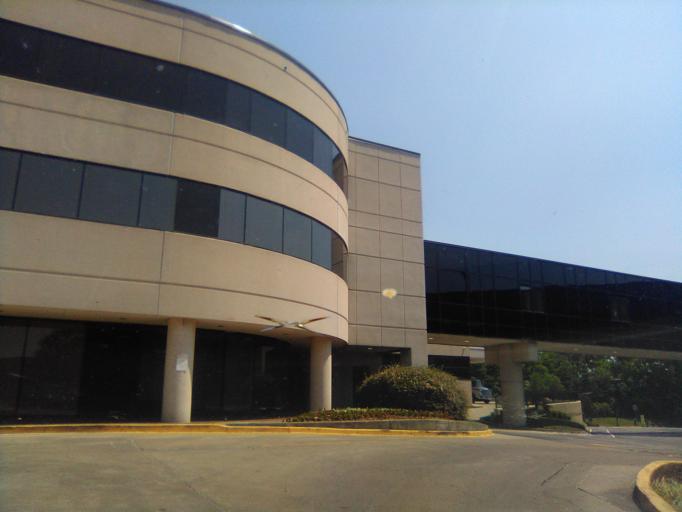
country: US
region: Tennessee
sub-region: Davidson County
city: Belle Meade
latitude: 36.1285
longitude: -86.8437
